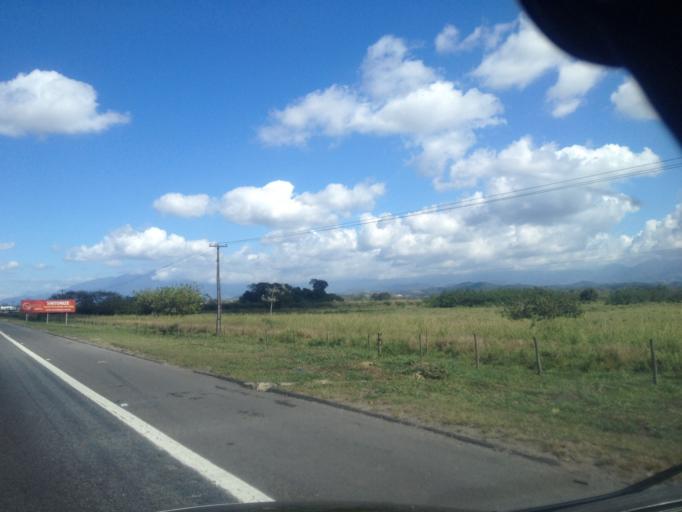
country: BR
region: Rio de Janeiro
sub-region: Porto Real
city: Porto Real
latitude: -22.4503
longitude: -44.3345
